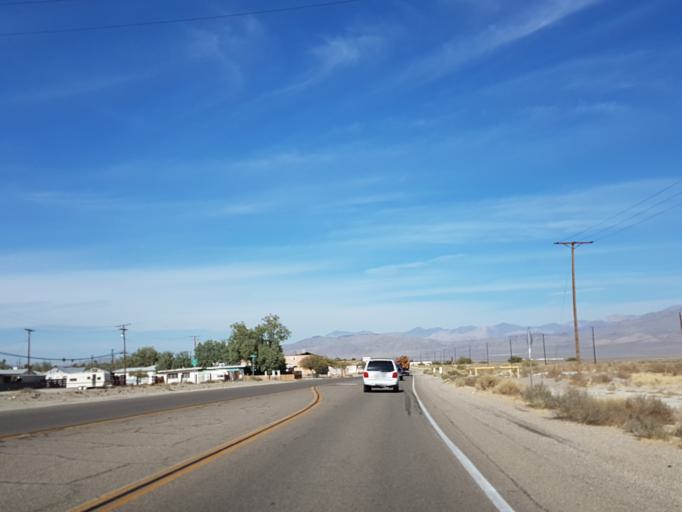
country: US
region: California
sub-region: San Bernardino County
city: Searles Valley
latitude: 35.7839
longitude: -117.3639
